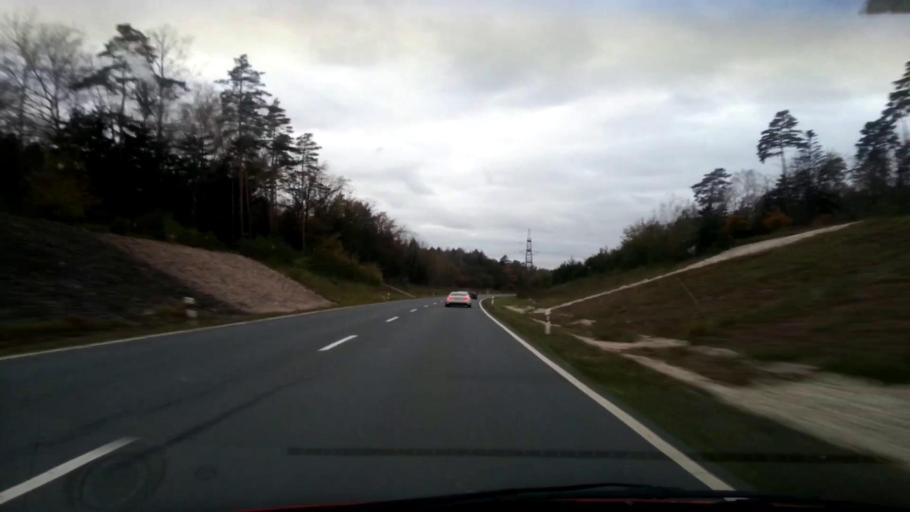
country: DE
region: Bavaria
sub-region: Upper Franconia
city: Schneckenlohe
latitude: 50.2078
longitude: 11.1675
